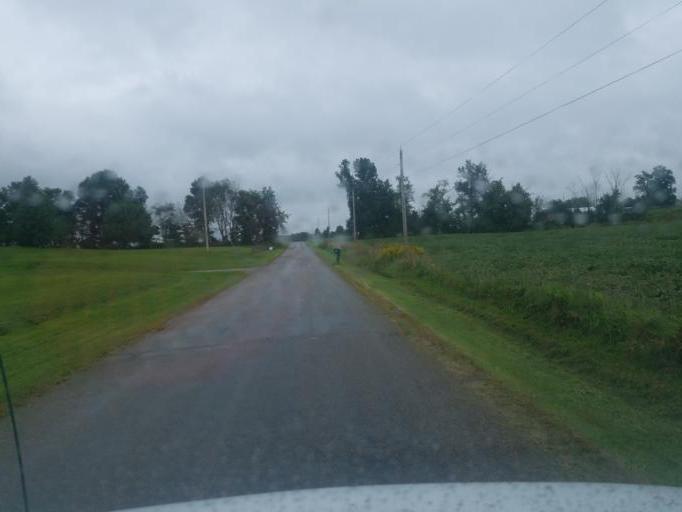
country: US
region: Ohio
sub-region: Wayne County
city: West Salem
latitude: 40.9216
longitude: -82.1186
